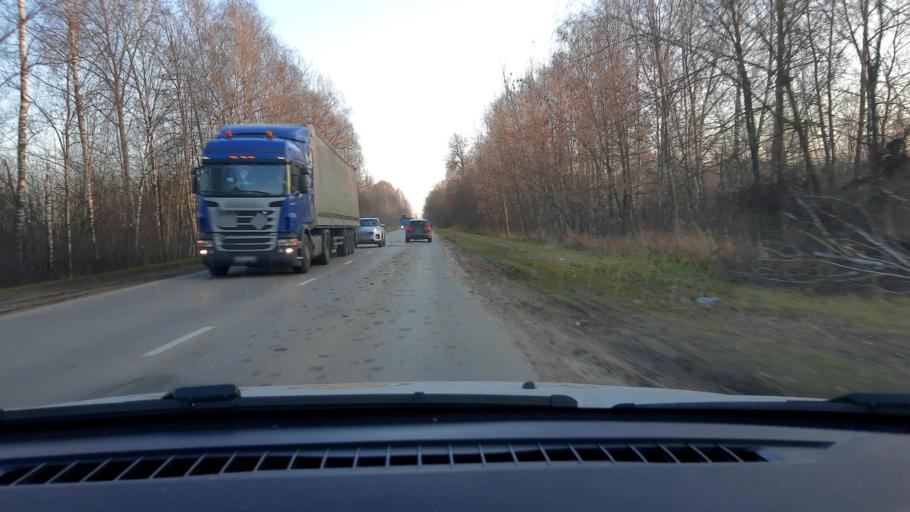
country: RU
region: Nizjnij Novgorod
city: Volodarsk
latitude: 56.2501
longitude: 43.1750
